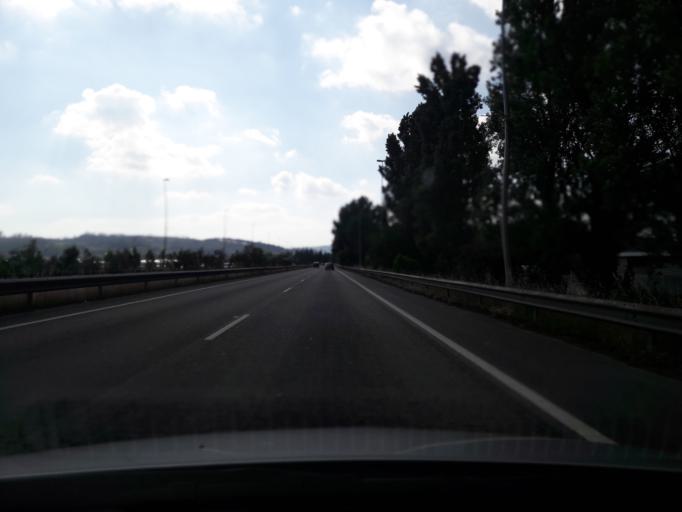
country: PT
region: Braga
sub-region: Guimaraes
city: Candoso
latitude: 41.4376
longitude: -8.3184
